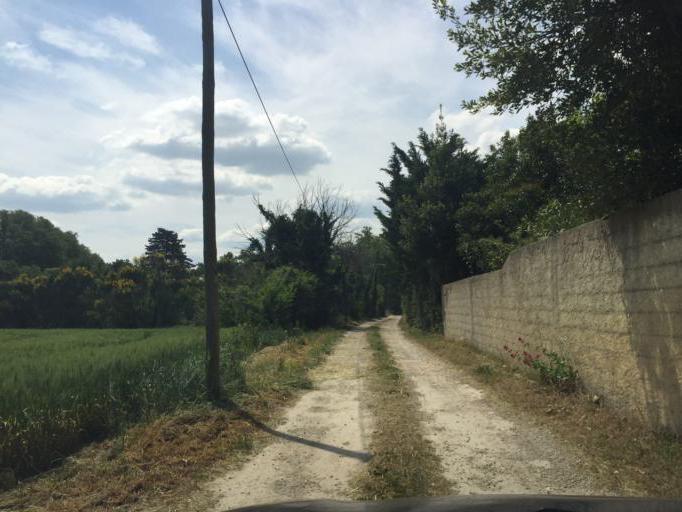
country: FR
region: Provence-Alpes-Cote d'Azur
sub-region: Departement du Vaucluse
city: Jonquieres
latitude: 44.1344
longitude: 4.9113
